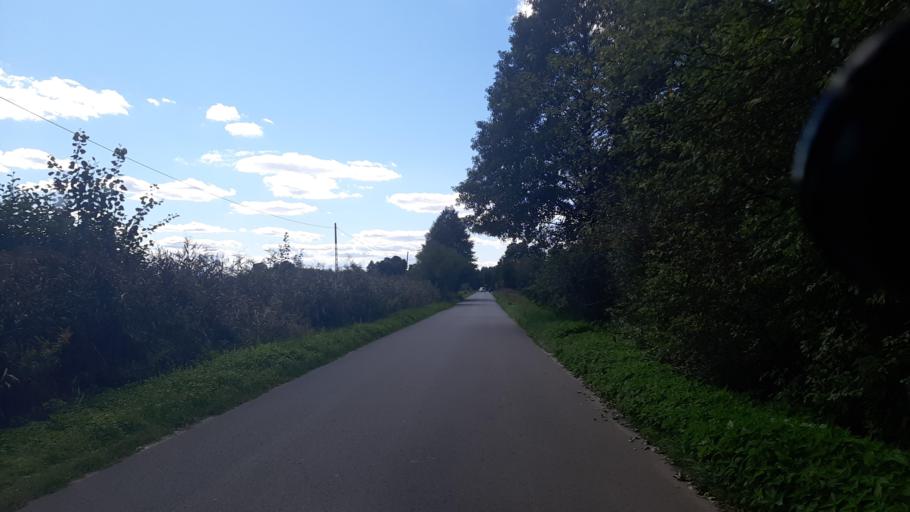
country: PL
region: Lublin Voivodeship
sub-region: Powiat lubelski
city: Garbow
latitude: 51.4048
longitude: 22.3596
